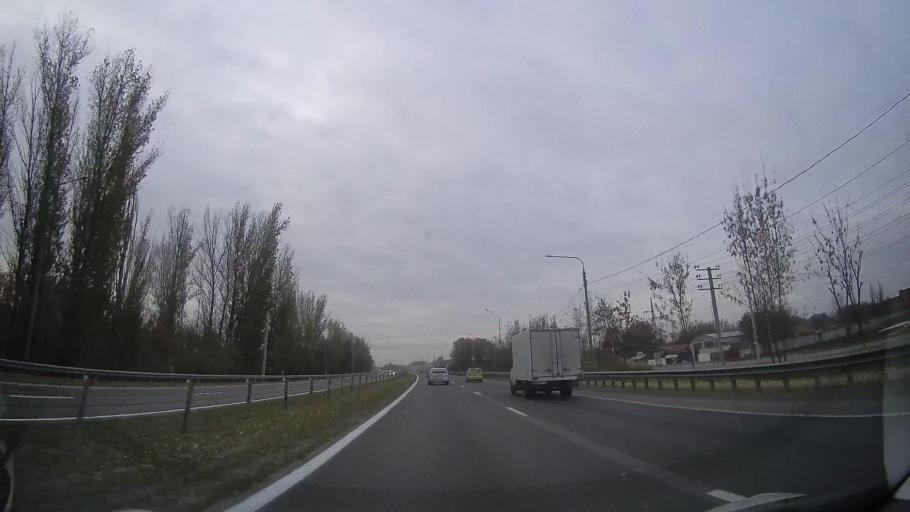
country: RU
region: Rostov
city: Bataysk
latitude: 47.1116
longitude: 39.7663
